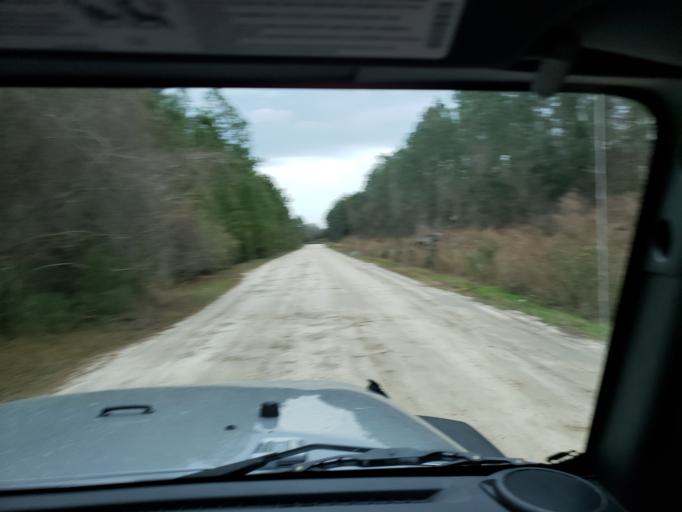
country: US
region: Georgia
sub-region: Chatham County
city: Bloomingdale
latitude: 32.0603
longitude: -81.3573
